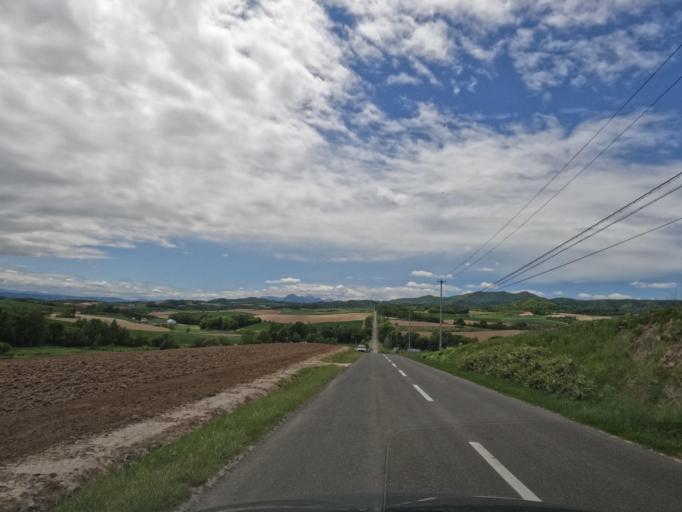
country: JP
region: Hokkaido
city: Shimo-furano
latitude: 43.5175
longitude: 142.4278
